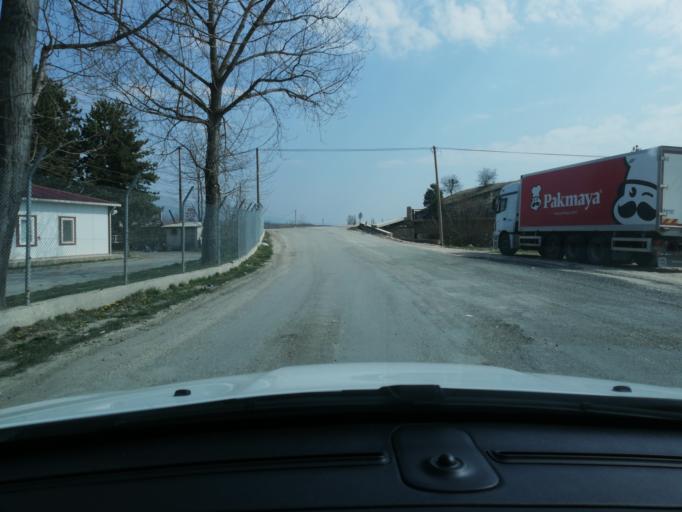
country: TR
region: Kastamonu
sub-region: Cide
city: Kastamonu
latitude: 41.4477
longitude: 33.7647
